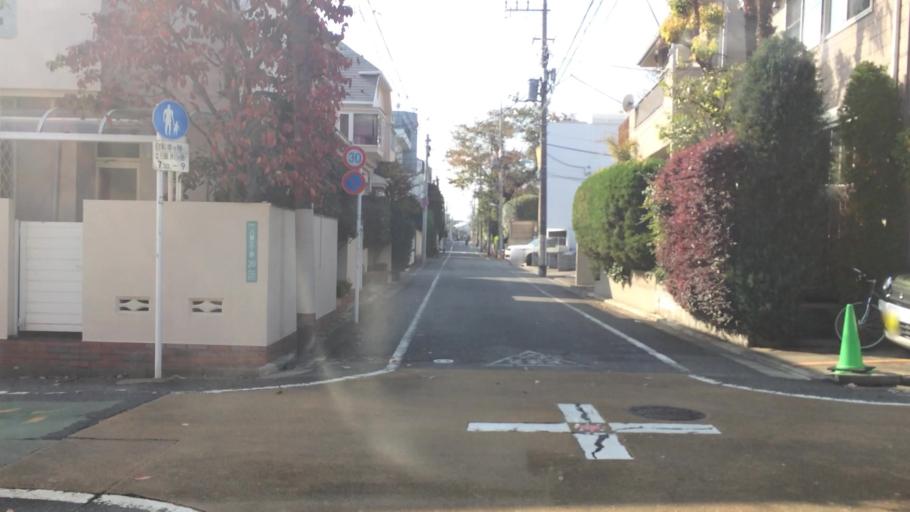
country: JP
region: Tokyo
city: Tokyo
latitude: 35.6171
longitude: 139.6660
